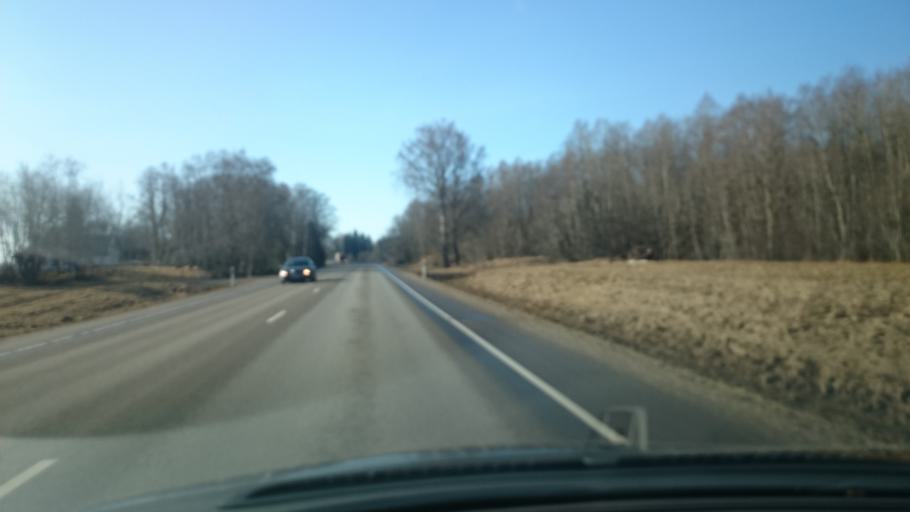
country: EE
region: Raplamaa
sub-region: Kohila vald
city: Kohila
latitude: 59.2586
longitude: 24.7409
